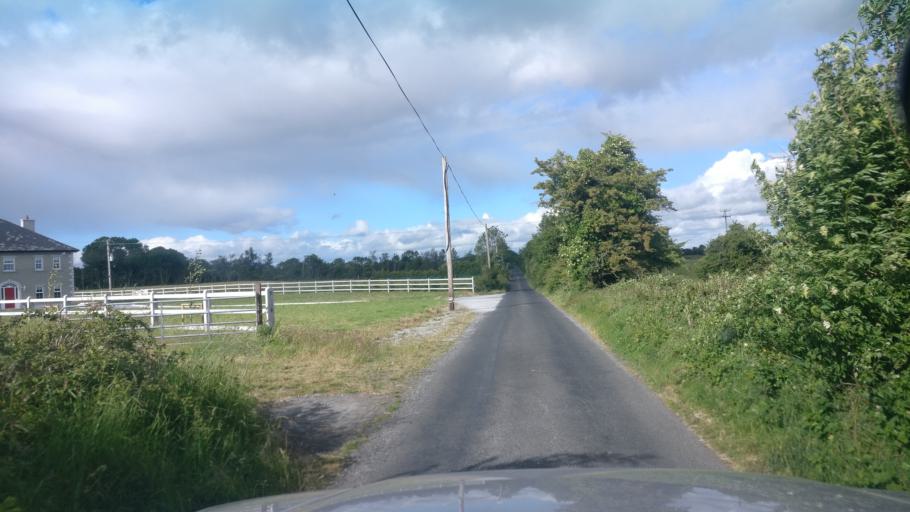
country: IE
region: Connaught
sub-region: County Galway
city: Loughrea
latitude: 53.1930
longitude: -8.3826
